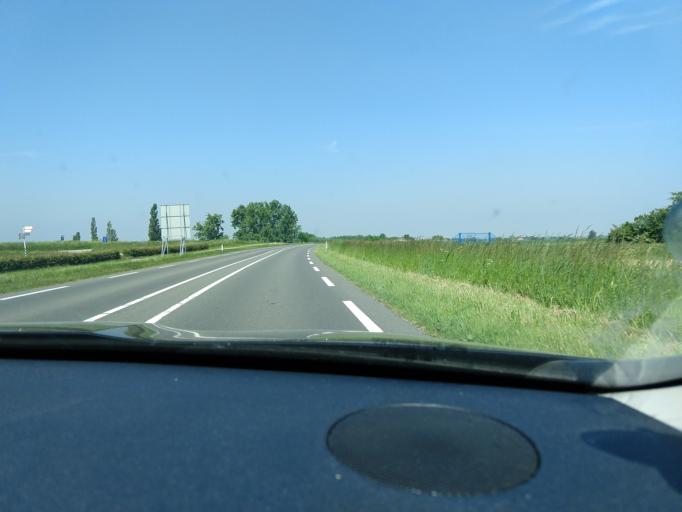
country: NL
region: Zeeland
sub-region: Gemeente Tholen
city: Tholen
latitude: 51.5429
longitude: 4.1347
